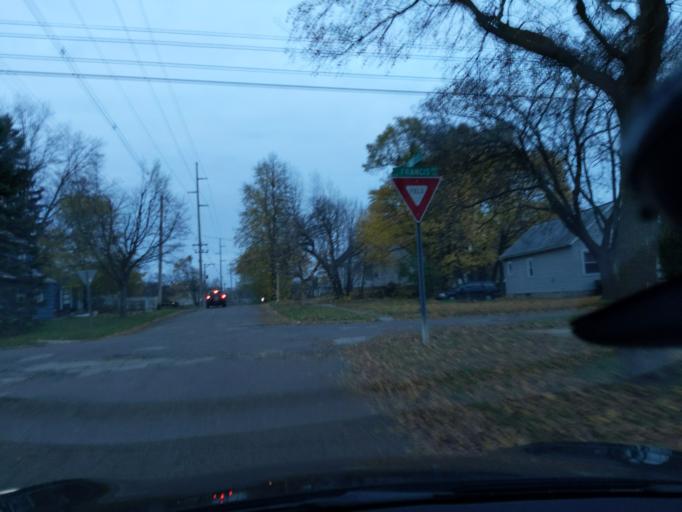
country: US
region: Michigan
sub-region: Ingham County
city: East Lansing
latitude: 42.7286
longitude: -84.5167
